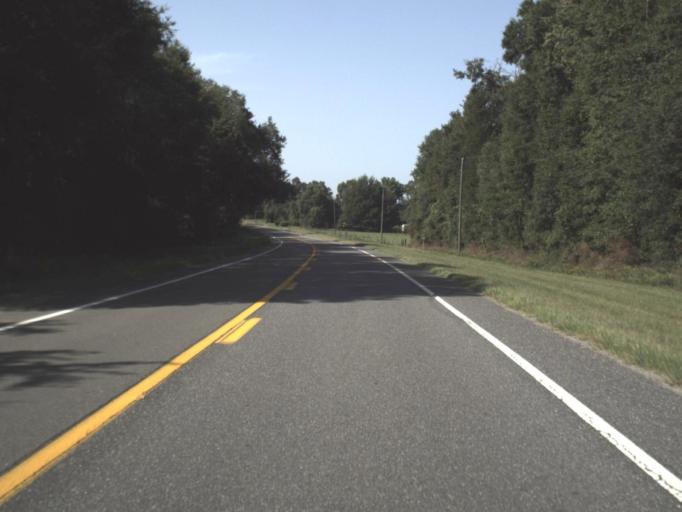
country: US
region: Florida
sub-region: Columbia County
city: Lake City
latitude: 30.0301
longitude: -82.7100
